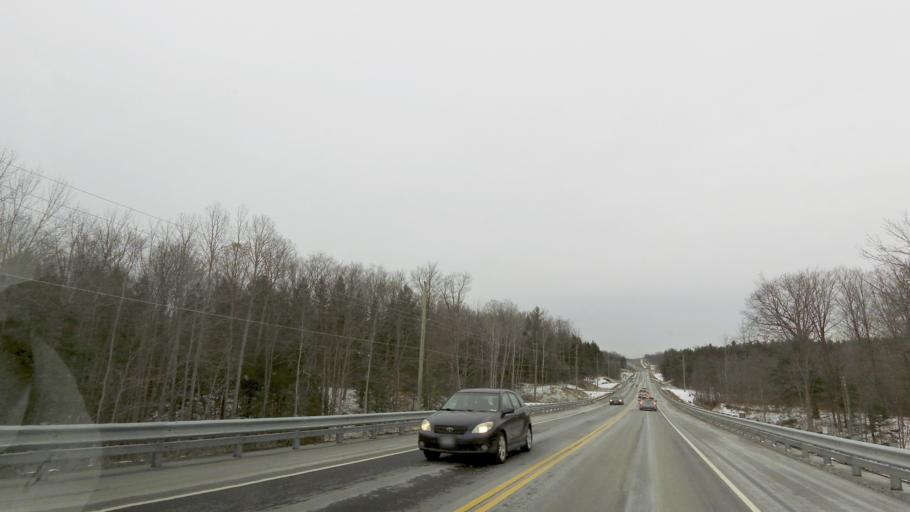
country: CA
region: Ontario
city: Newmarket
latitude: 44.0764
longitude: -79.5131
